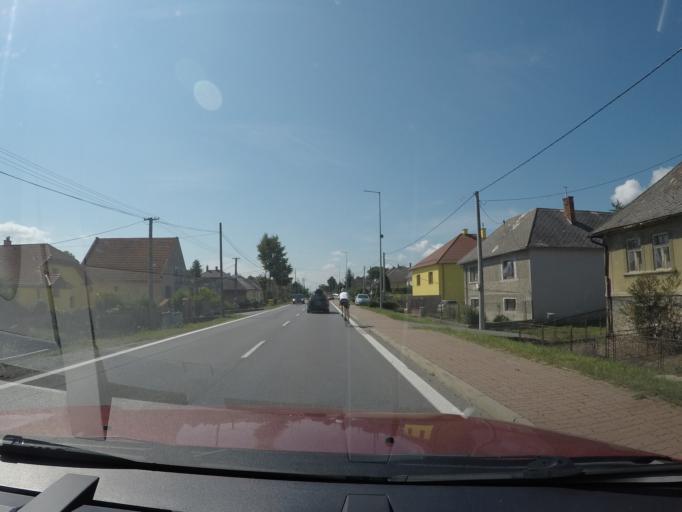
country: SK
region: Presovsky
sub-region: Okres Presov
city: Presov
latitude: 48.9291
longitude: 21.2410
